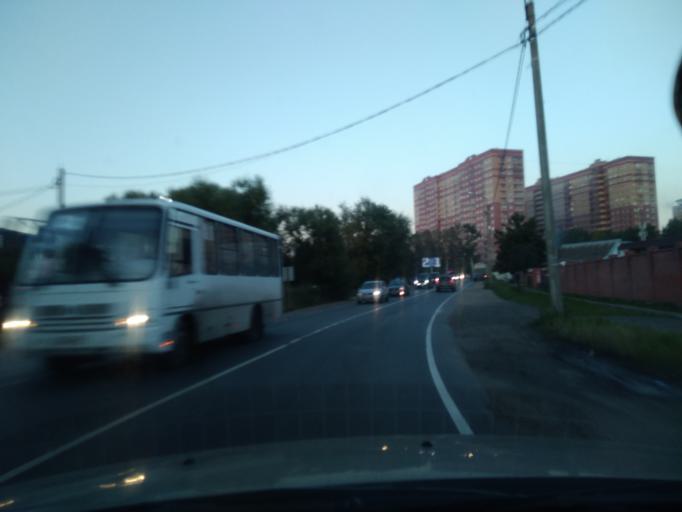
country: RU
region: Moscow
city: Strogino
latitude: 55.8629
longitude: 37.3865
